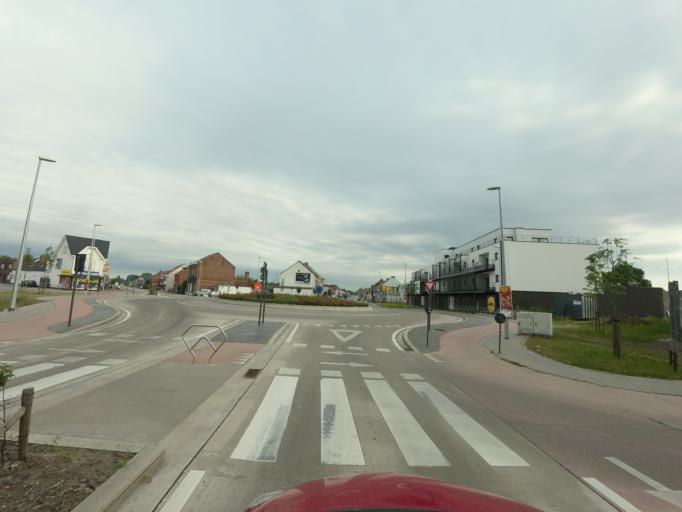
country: BE
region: Flanders
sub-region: Provincie Limburg
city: Leopoldsburg
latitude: 51.1243
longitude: 5.2570
